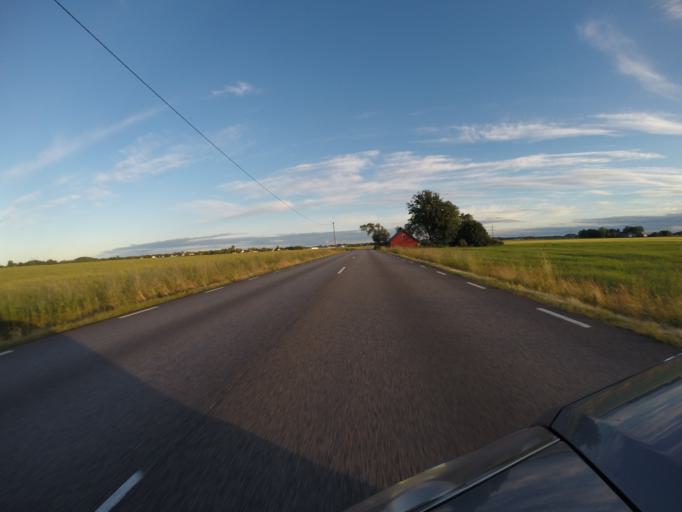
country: SE
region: Skane
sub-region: Bjuvs Kommun
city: Bjuv
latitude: 56.0950
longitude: 12.8909
